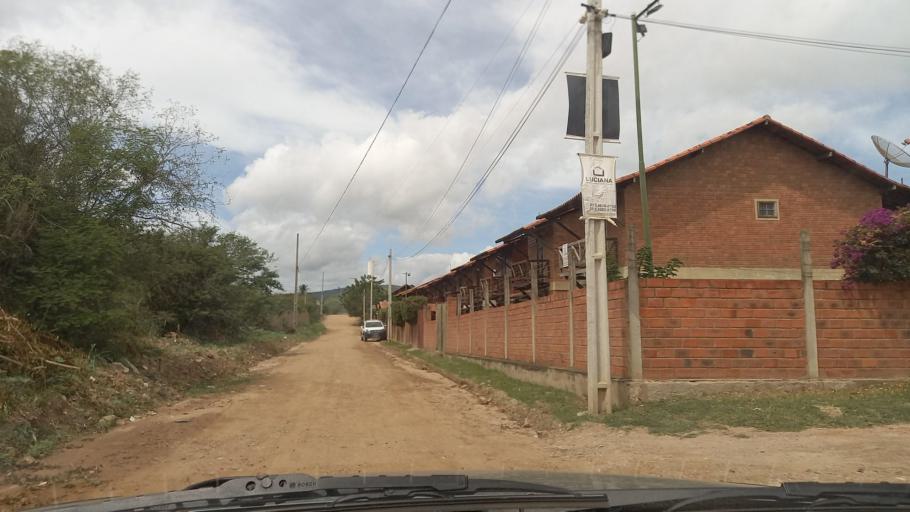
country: BR
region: Pernambuco
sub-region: Gravata
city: Gravata
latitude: -8.1919
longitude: -35.5933
